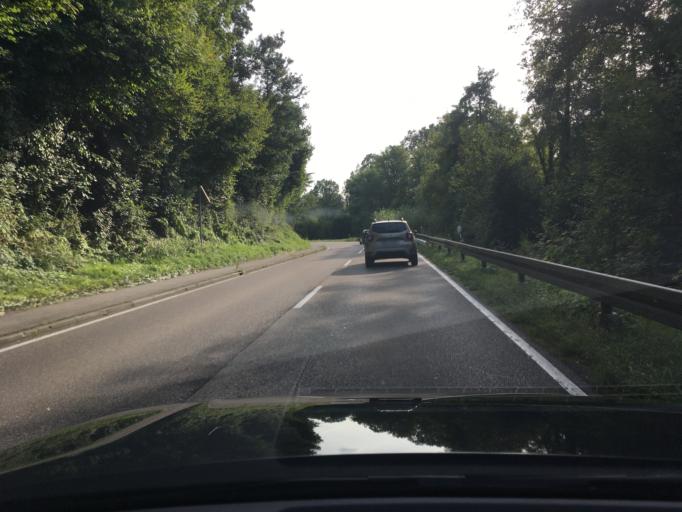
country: DE
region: Baden-Wuerttemberg
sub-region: Regierungsbezirk Stuttgart
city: Steinheim am der Murr
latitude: 48.9736
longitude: 9.2881
